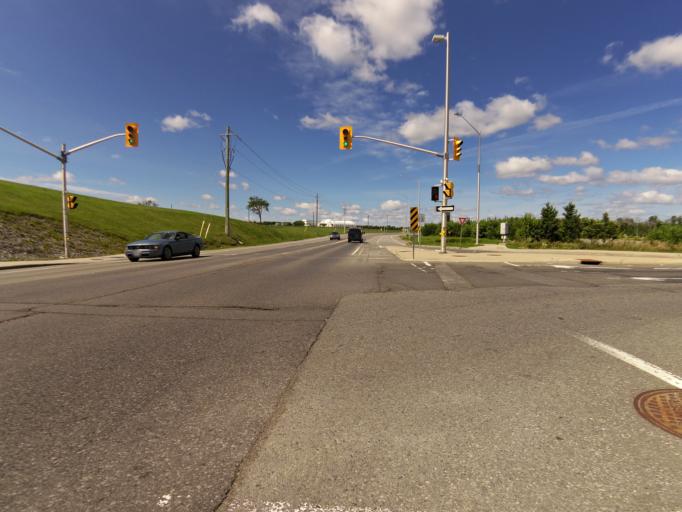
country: CA
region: Ontario
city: Ottawa
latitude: 45.3292
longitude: -75.6538
